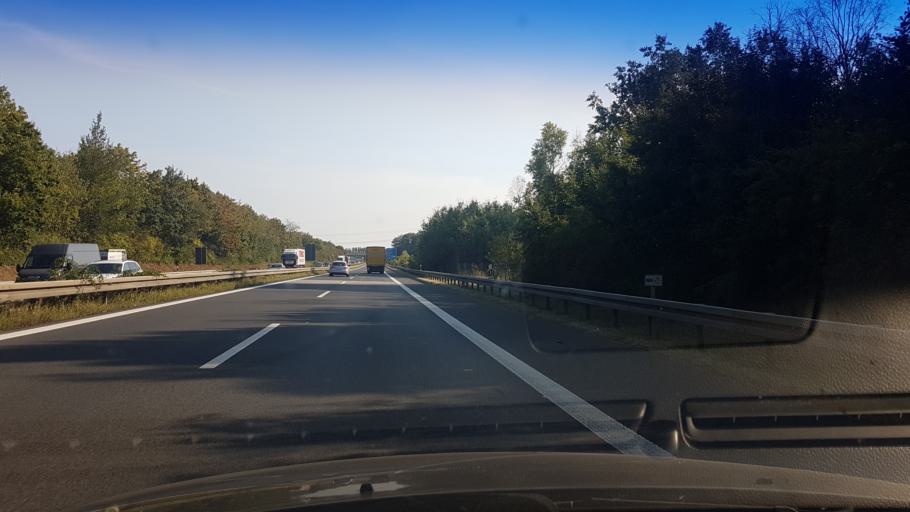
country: DE
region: Bavaria
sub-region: Upper Franconia
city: Gundelsheim
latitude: 49.9391
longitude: 10.9068
